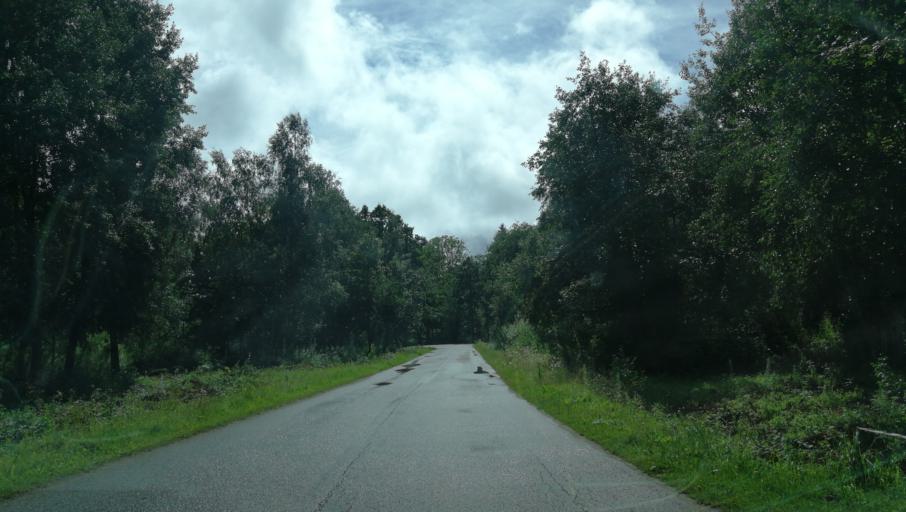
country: LV
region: Cesu Rajons
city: Cesis
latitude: 57.2970
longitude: 25.2608
